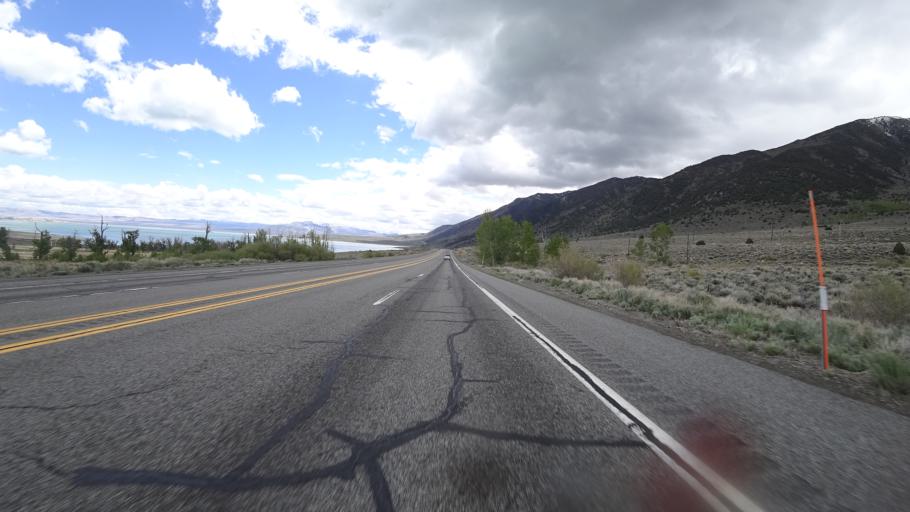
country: US
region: California
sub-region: Mono County
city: Bridgeport
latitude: 38.0193
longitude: -119.1574
